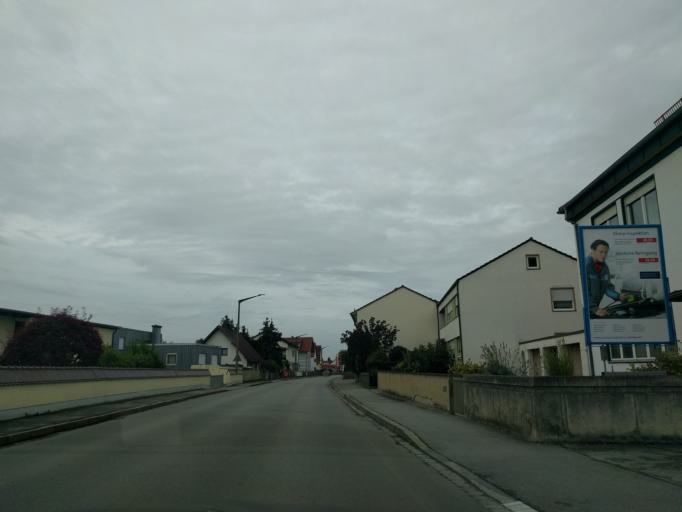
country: DE
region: Bavaria
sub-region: Lower Bavaria
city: Plattling
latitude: 48.7751
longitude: 12.8684
